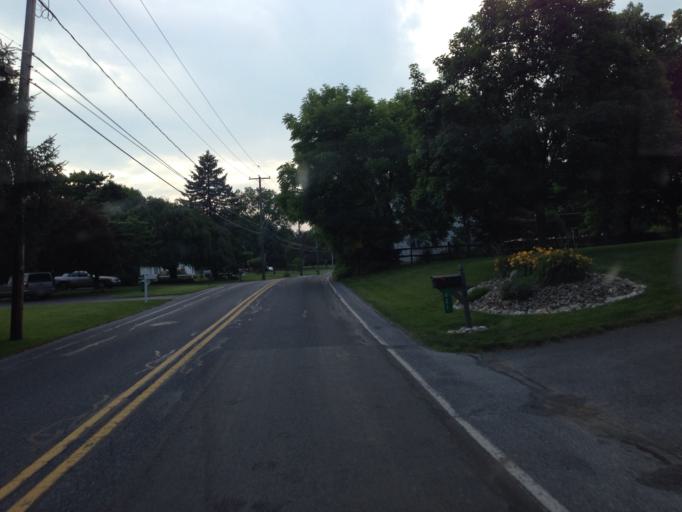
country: US
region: Pennsylvania
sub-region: Lancaster County
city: Rothsville
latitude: 40.1439
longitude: -76.2771
